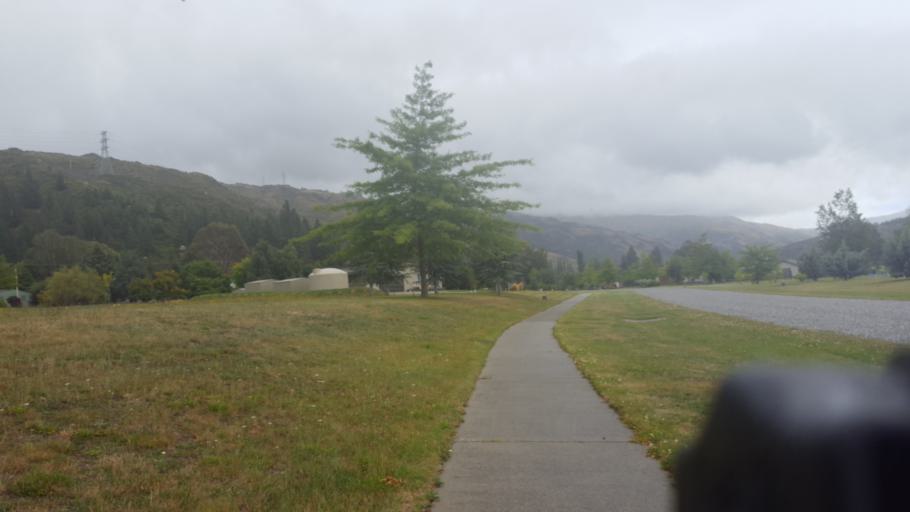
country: NZ
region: Otago
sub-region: Queenstown-Lakes District
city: Wanaka
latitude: -45.1961
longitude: 169.3167
